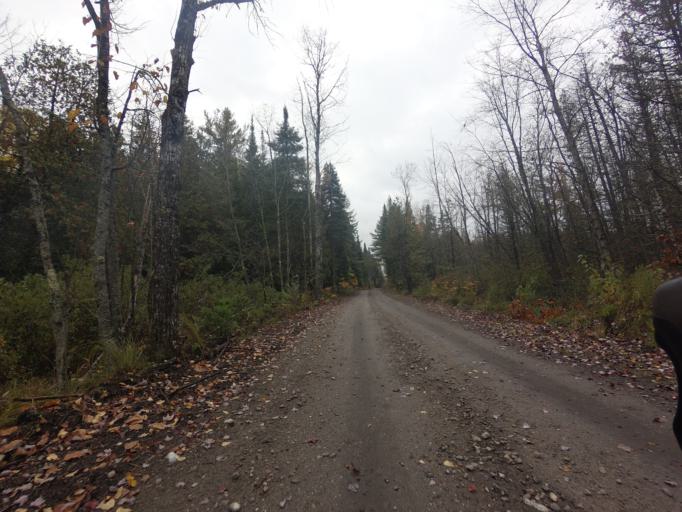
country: CA
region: Ontario
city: Renfrew
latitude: 45.1713
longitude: -76.6806
